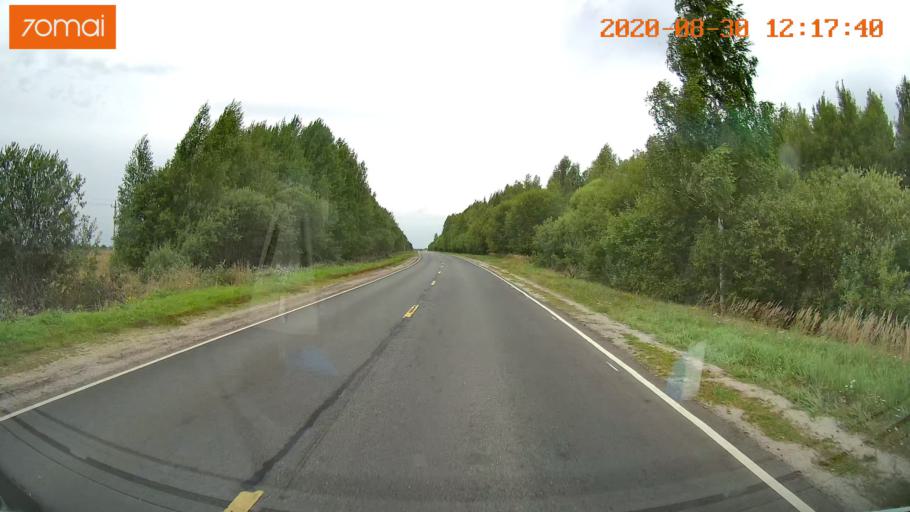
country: RU
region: Ivanovo
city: Yur'yevets
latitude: 57.3237
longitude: 42.9720
